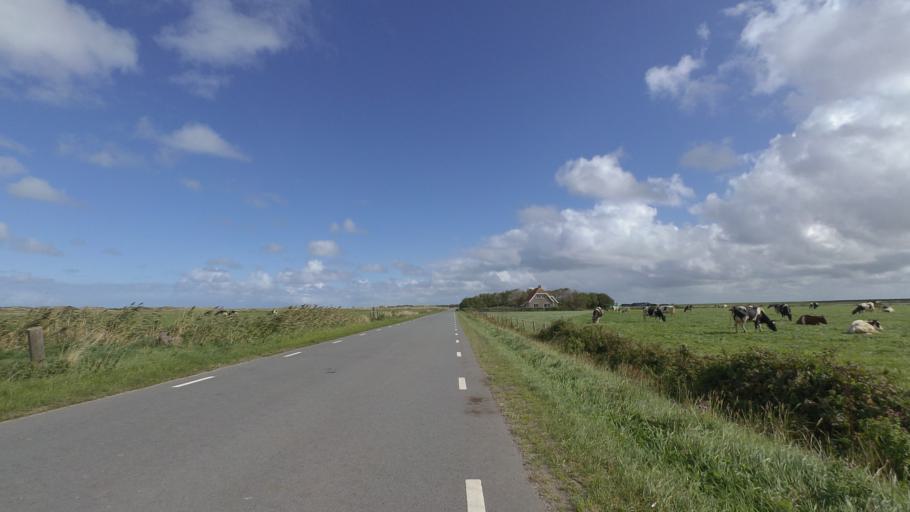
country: NL
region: Friesland
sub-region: Gemeente Ameland
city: Nes
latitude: 53.4500
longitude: 5.8246
